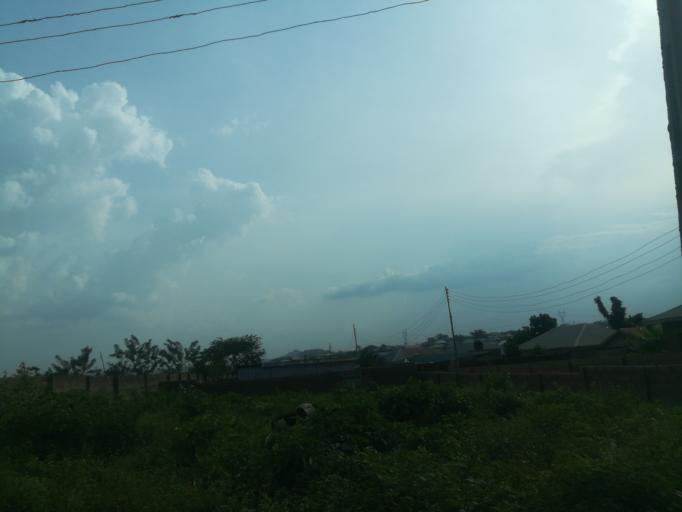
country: NG
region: Oyo
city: Moniya
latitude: 7.5264
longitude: 3.9290
